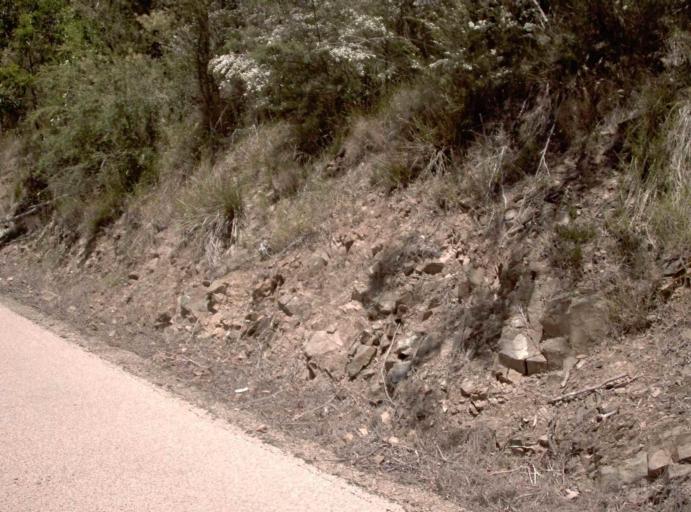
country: AU
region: Victoria
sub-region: East Gippsland
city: Bairnsdale
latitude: -37.4630
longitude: 147.8315
